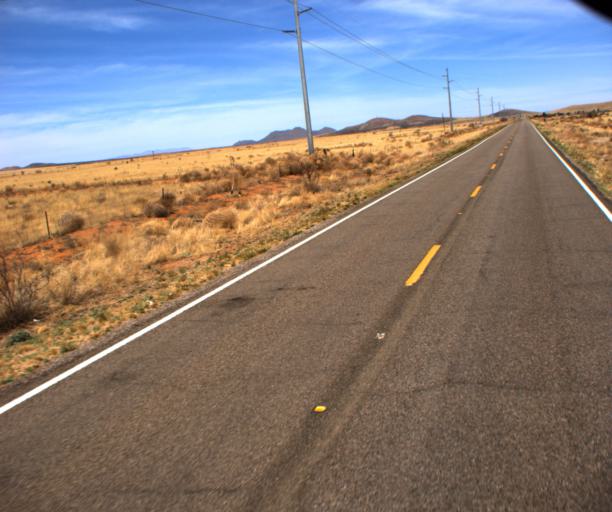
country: US
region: Arizona
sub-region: Cochise County
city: Tombstone
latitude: 31.8596
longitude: -109.6951
